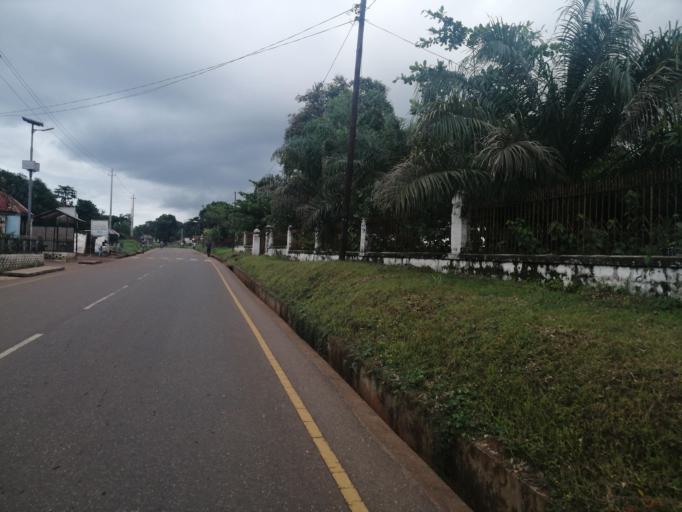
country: SL
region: Northern Province
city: Port Loko
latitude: 8.7678
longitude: -12.7825
